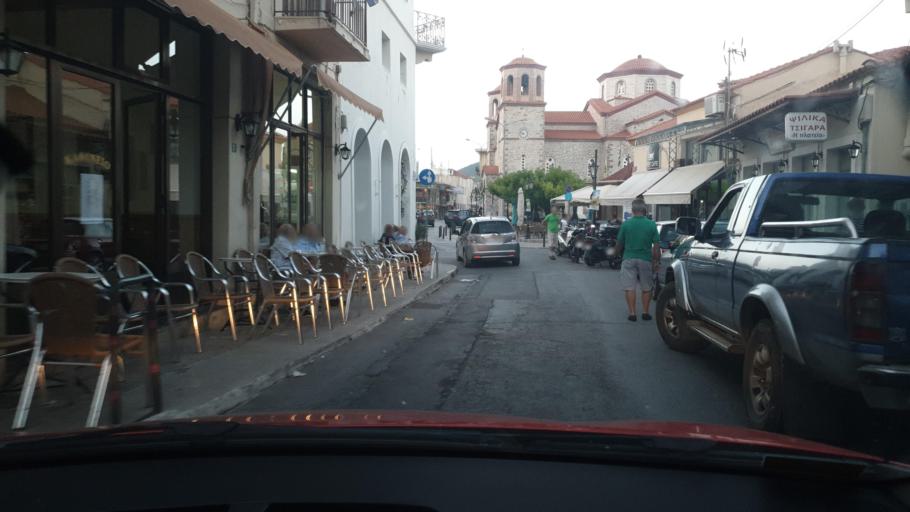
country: GR
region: Central Greece
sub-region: Nomos Evvoias
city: Kymi
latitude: 38.6319
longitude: 24.1038
